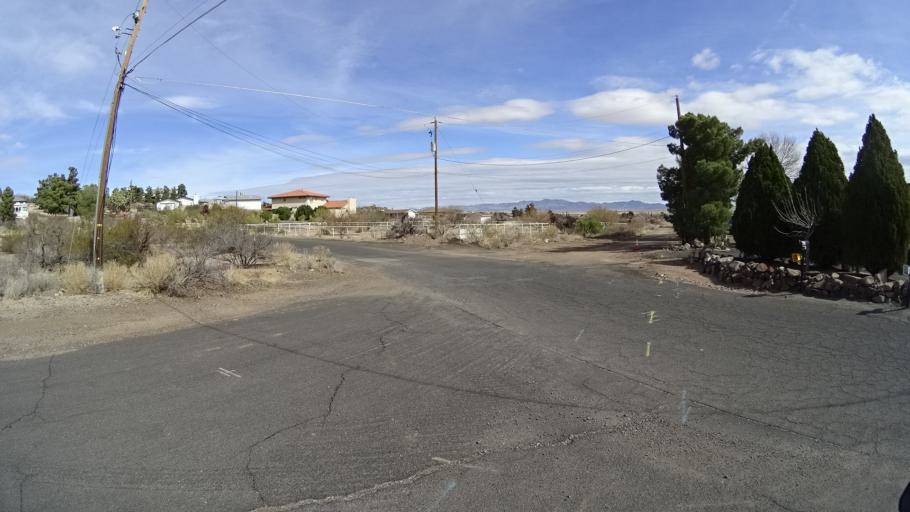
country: US
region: Arizona
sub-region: Mohave County
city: New Kingman-Butler
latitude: 35.2314
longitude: -114.0538
